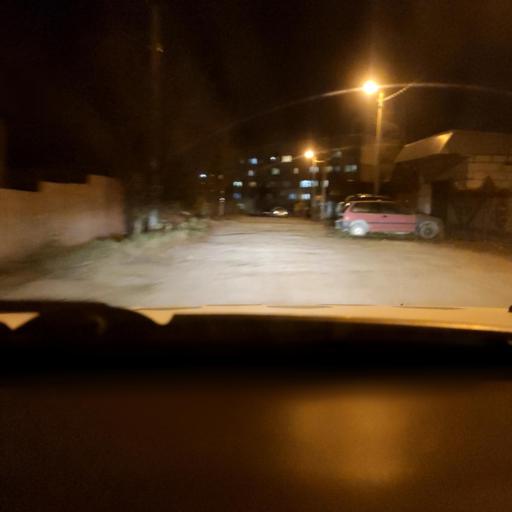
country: RU
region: Perm
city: Kondratovo
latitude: 57.9610
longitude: 56.1517
